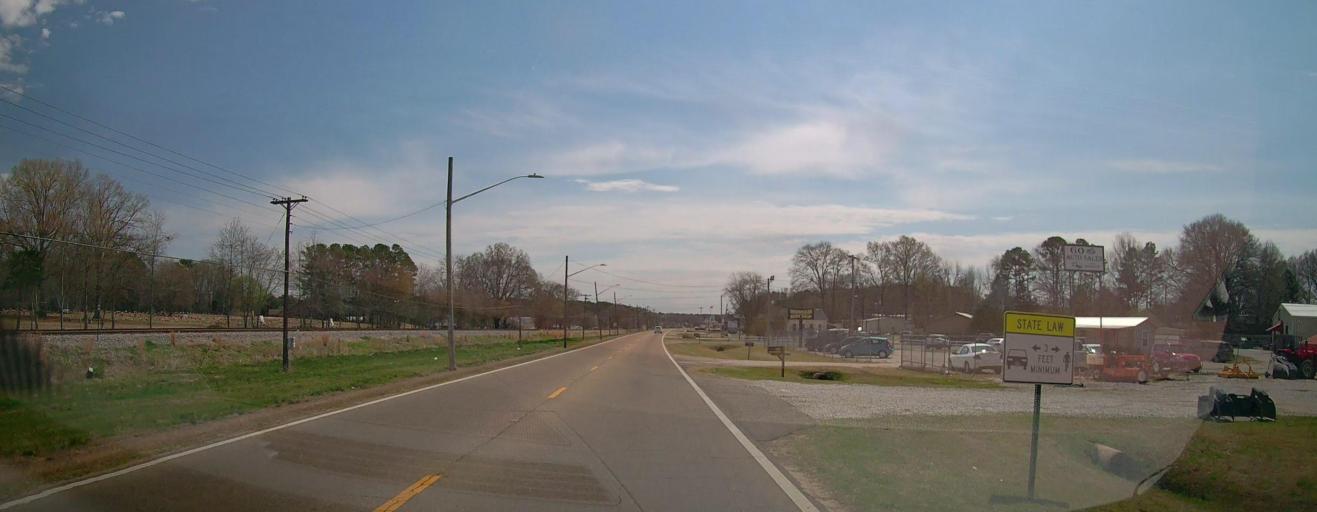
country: US
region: Mississippi
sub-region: Union County
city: New Albany
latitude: 34.5068
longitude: -89.0315
